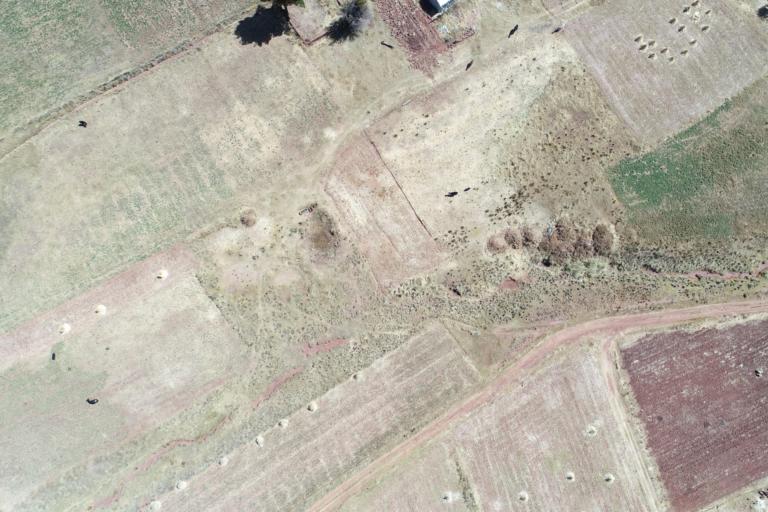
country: BO
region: La Paz
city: Tiahuanaco
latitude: -16.6015
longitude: -68.7730
